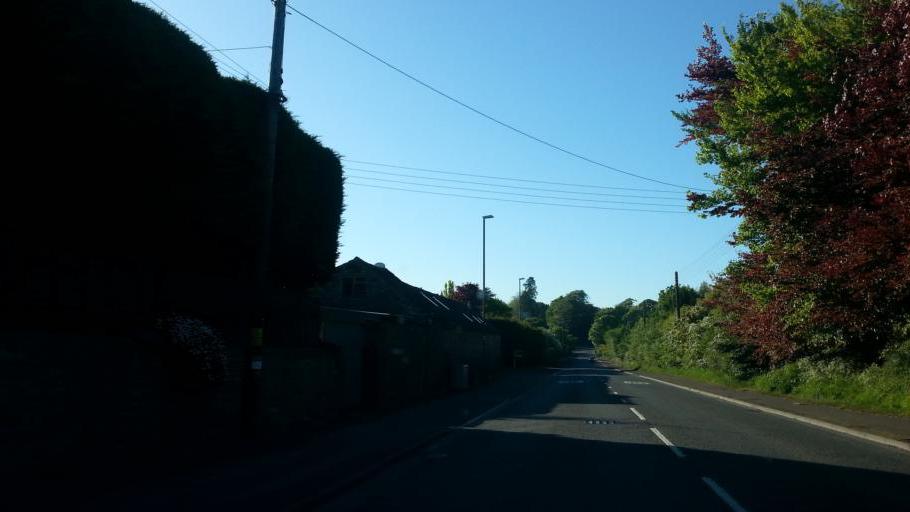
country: GB
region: England
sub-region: Bath and North East Somerset
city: Clutton
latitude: 51.3233
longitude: -2.5458
